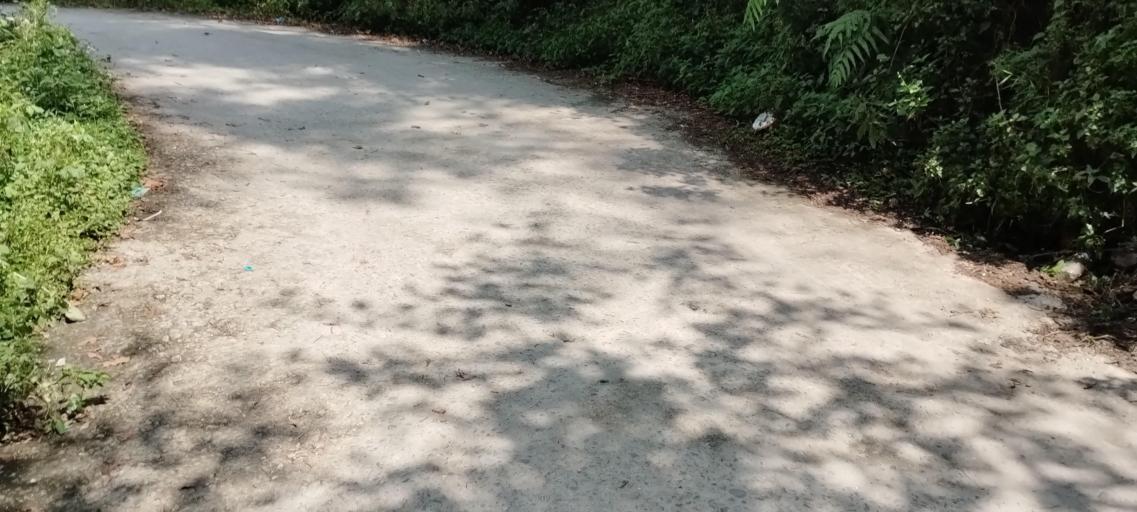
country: NP
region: Central Region
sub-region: Bagmati Zone
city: Kathmandu
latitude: 27.7891
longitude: 85.3613
